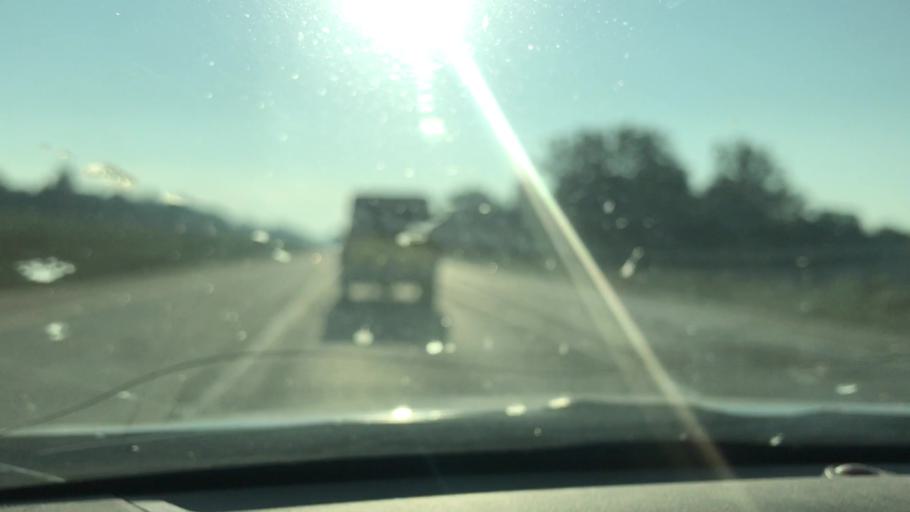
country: US
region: Michigan
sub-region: Livingston County
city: Howell
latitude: 42.6100
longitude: -83.9800
